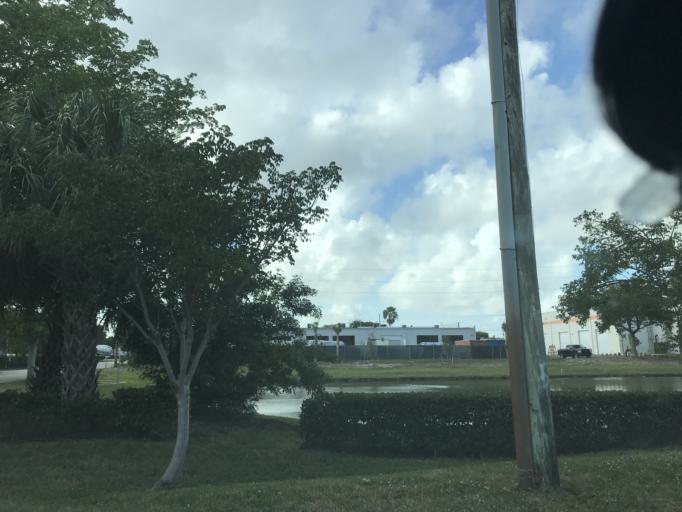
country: US
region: Florida
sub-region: Palm Beach County
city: Delray Beach
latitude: 26.4678
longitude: -80.0920
